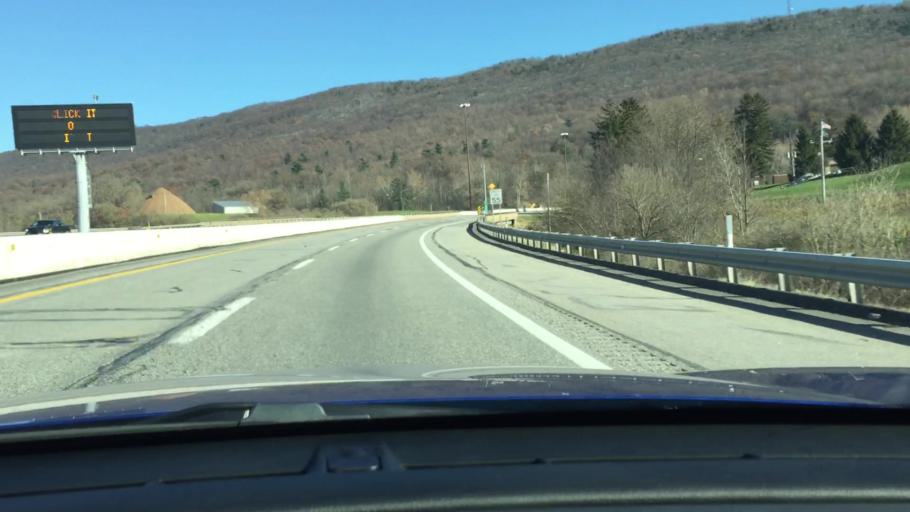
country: US
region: Pennsylvania
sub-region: Franklin County
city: Doylestown
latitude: 40.0912
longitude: -77.8614
